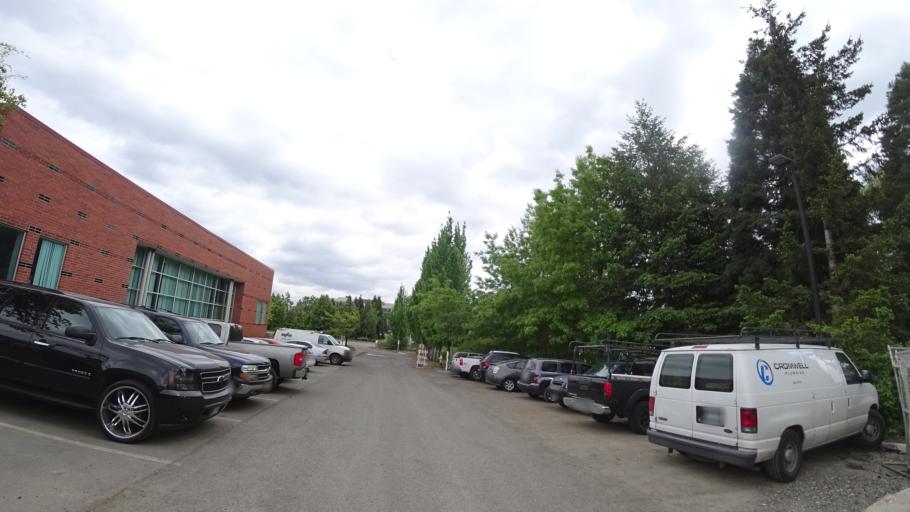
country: US
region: Oregon
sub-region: Washington County
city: Rockcreek
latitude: 45.5353
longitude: -122.8828
